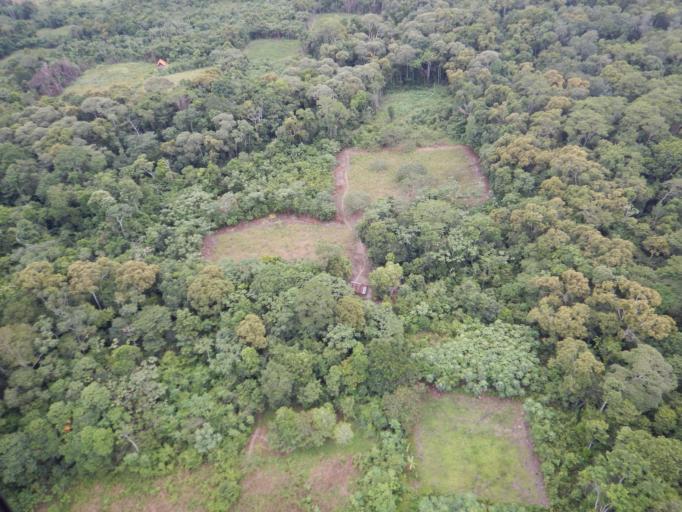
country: BO
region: Cochabamba
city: Chimore
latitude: -17.0051
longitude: -65.0090
